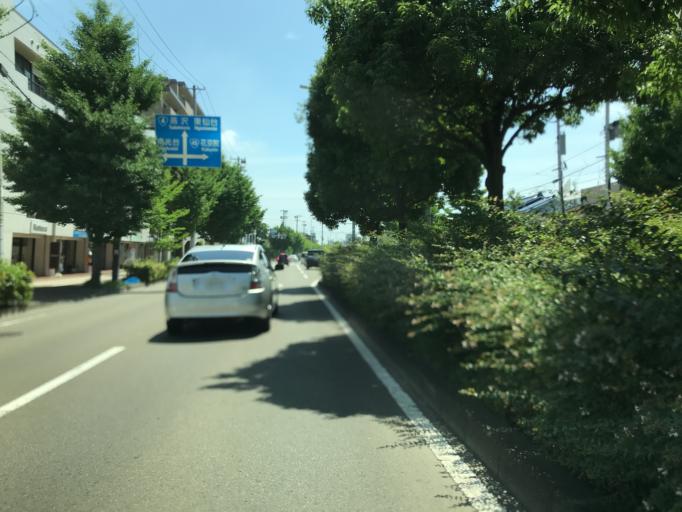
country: JP
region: Miyagi
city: Sendai-shi
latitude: 38.2743
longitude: 140.8830
